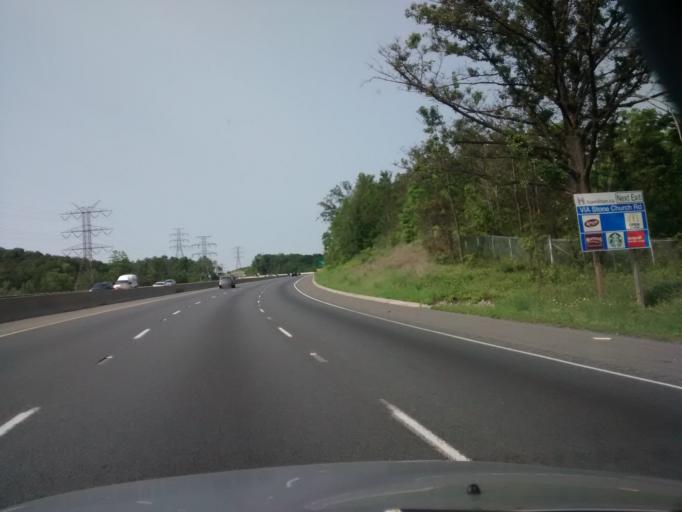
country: CA
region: Ontario
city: Hamilton
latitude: 43.2088
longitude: -79.8055
